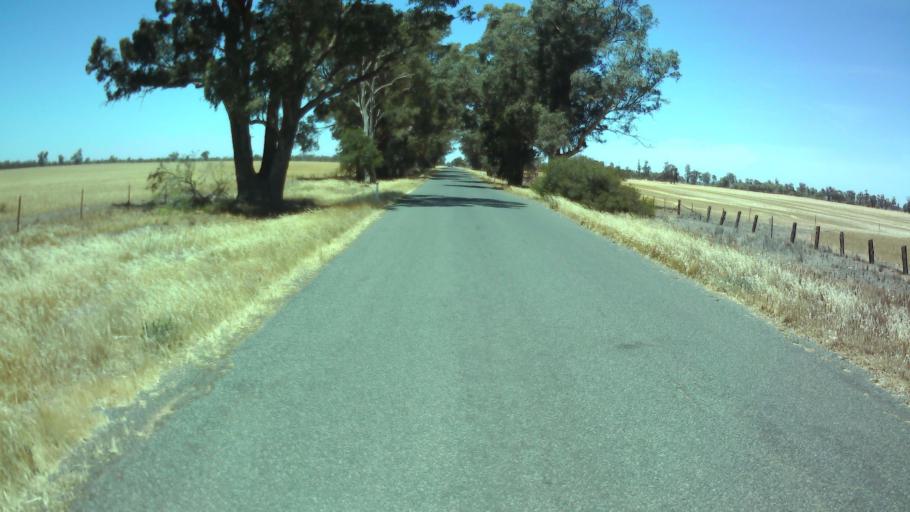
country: AU
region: New South Wales
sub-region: Weddin
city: Grenfell
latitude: -34.0222
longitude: 147.7924
